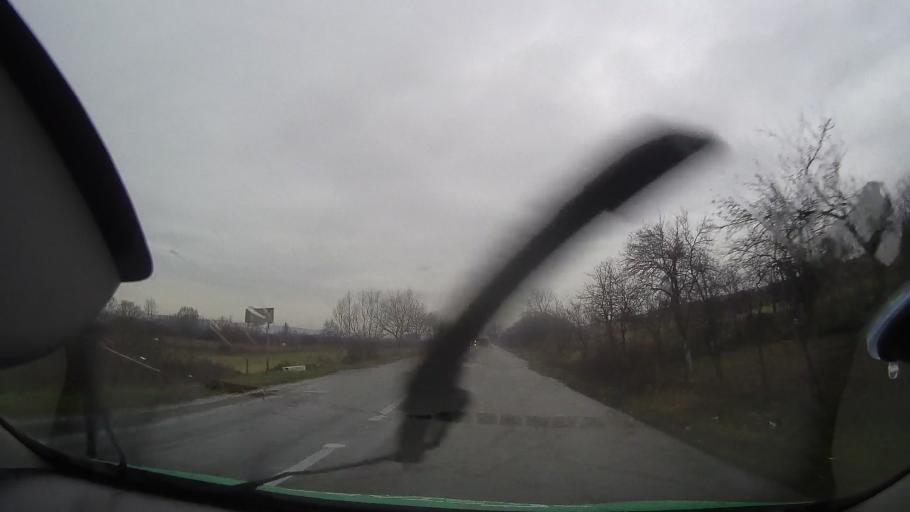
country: RO
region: Bihor
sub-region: Comuna Sambata
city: Sambata
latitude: 46.7758
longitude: 22.1873
